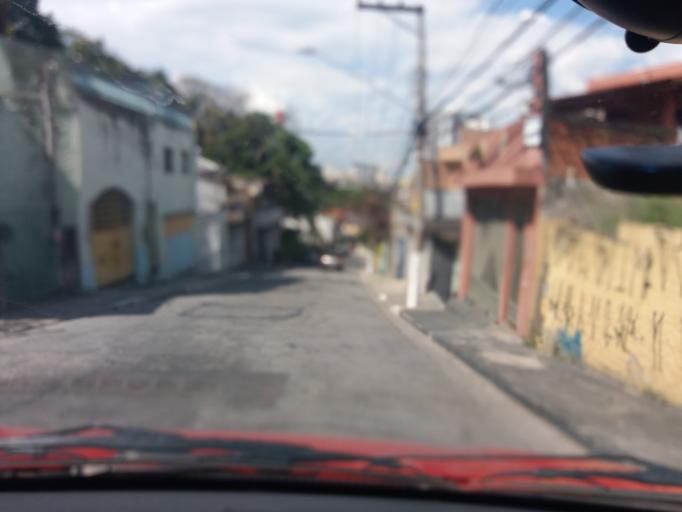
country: BR
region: Sao Paulo
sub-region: Taboao Da Serra
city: Taboao da Serra
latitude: -23.5924
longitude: -46.7434
